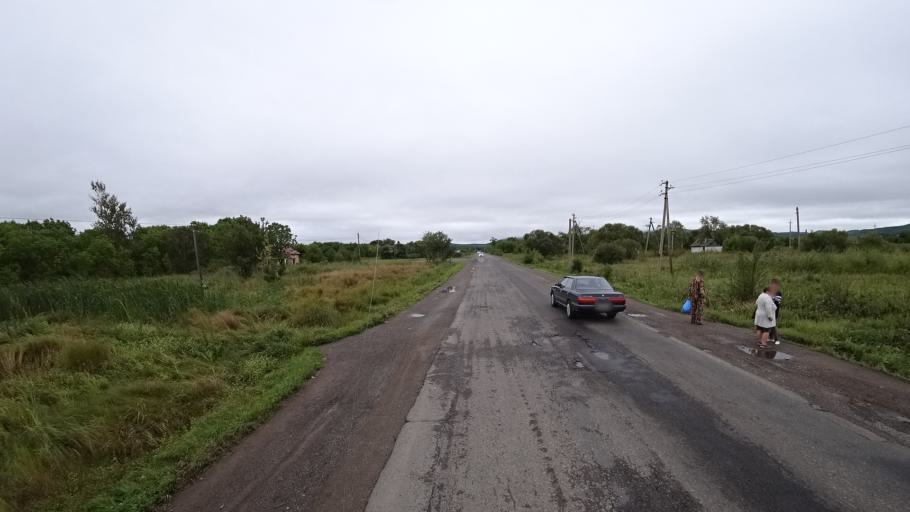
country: RU
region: Primorskiy
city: Monastyrishche
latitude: 44.1954
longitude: 132.4795
